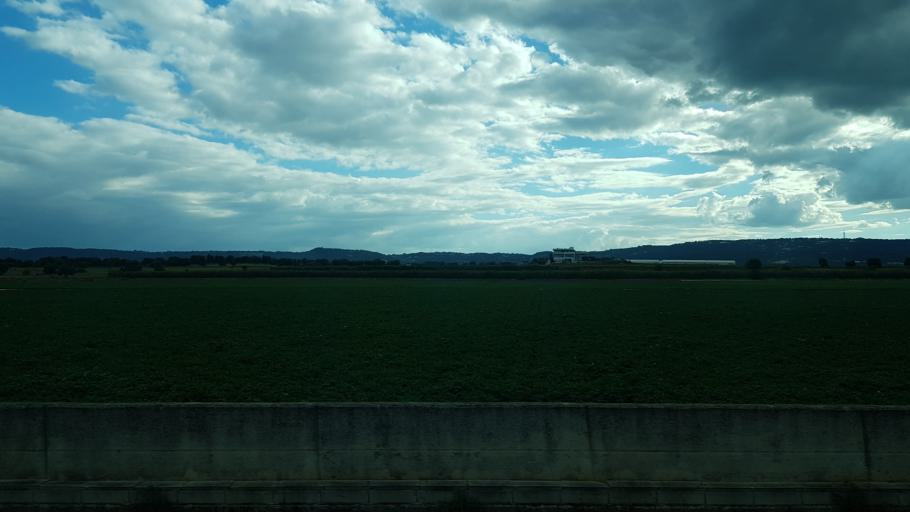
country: IT
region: Apulia
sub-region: Provincia di Brindisi
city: Fasano
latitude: 40.8461
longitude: 17.3941
